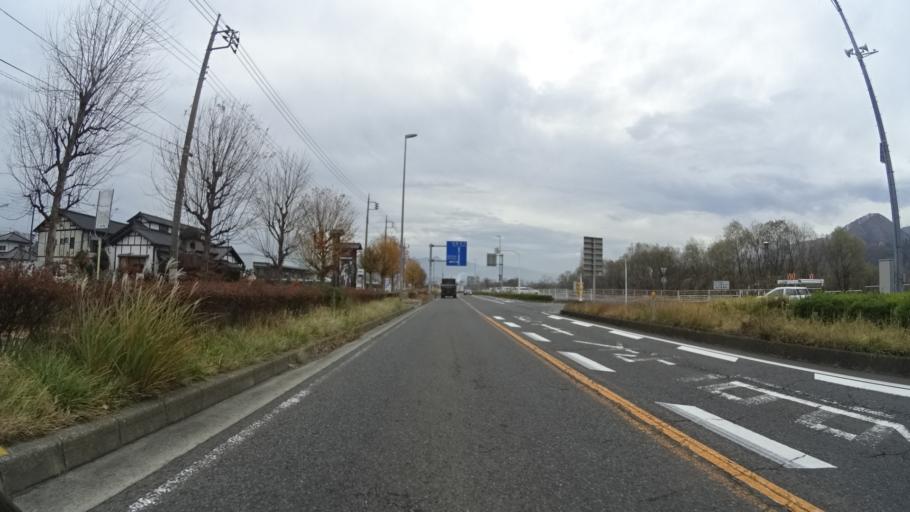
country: JP
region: Gunma
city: Numata
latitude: 36.6644
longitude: 139.0124
